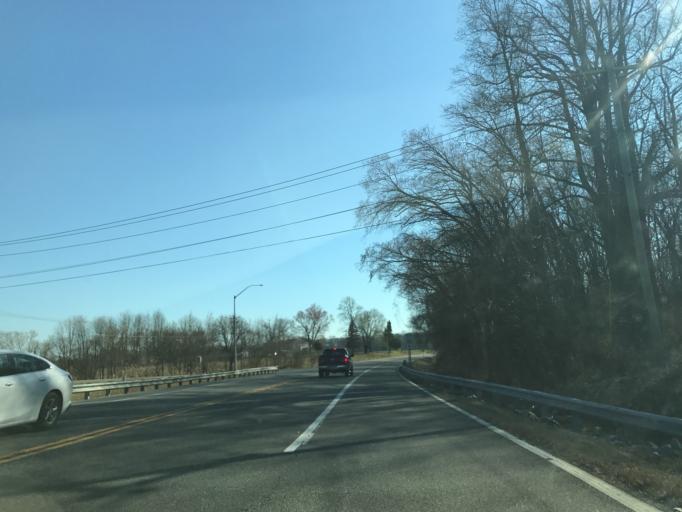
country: US
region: Maryland
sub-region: Queen Anne's County
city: Centreville
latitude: 39.0013
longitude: -76.0734
